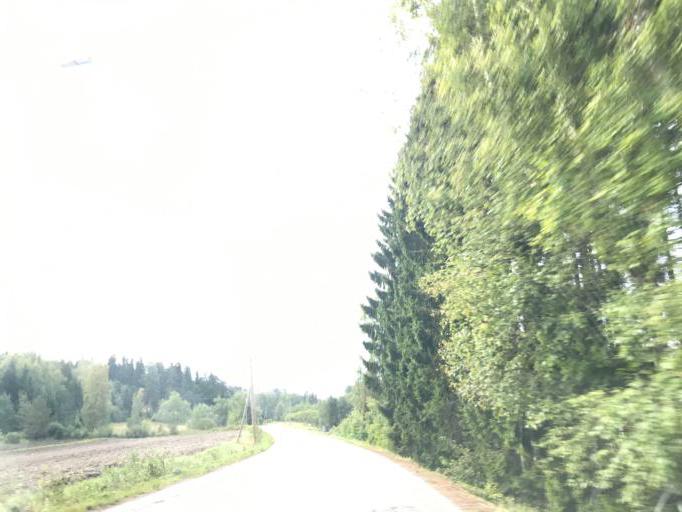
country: FI
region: Uusimaa
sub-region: Helsinki
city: Vihti
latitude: 60.3964
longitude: 24.5104
